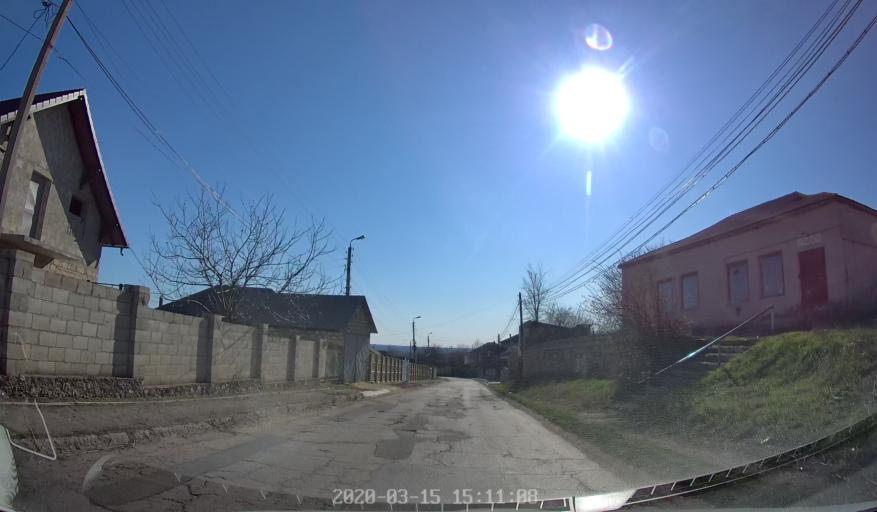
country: MD
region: Orhei
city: Orhei
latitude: 47.2642
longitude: 28.7785
